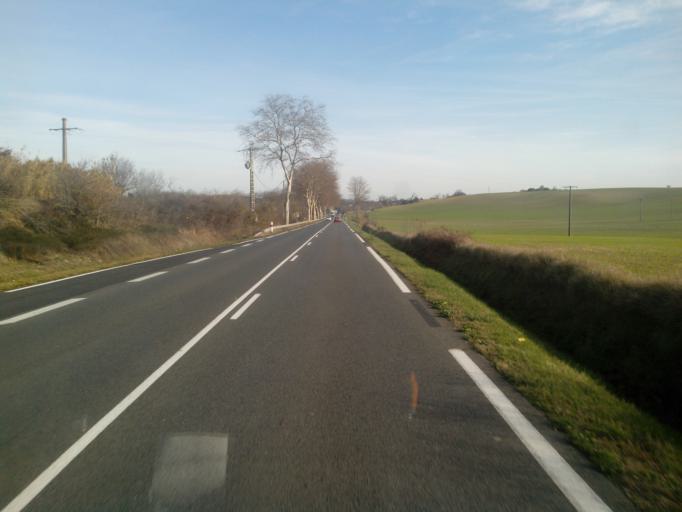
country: FR
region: Languedoc-Roussillon
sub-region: Departement de l'Aude
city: Villepinte
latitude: 43.2895
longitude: 2.0552
